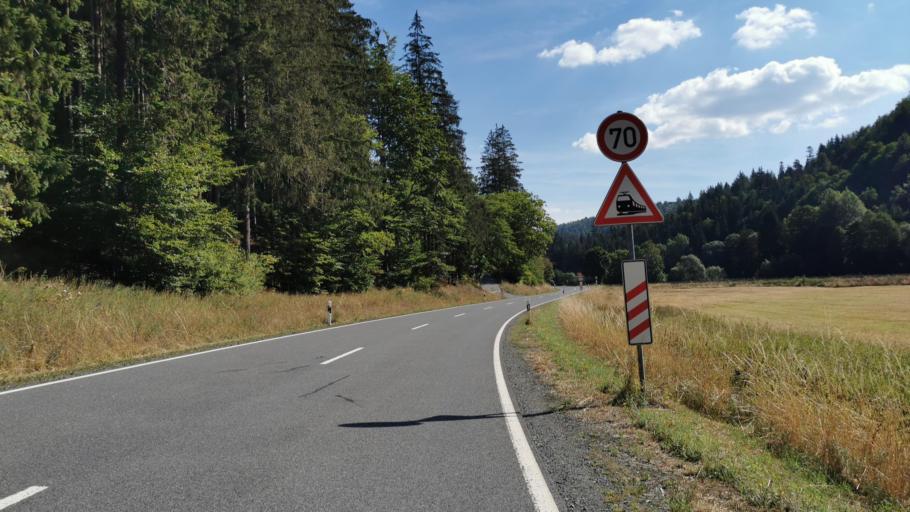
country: DE
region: Bavaria
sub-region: Upper Franconia
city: Nordhalben
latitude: 50.3278
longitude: 11.4997
